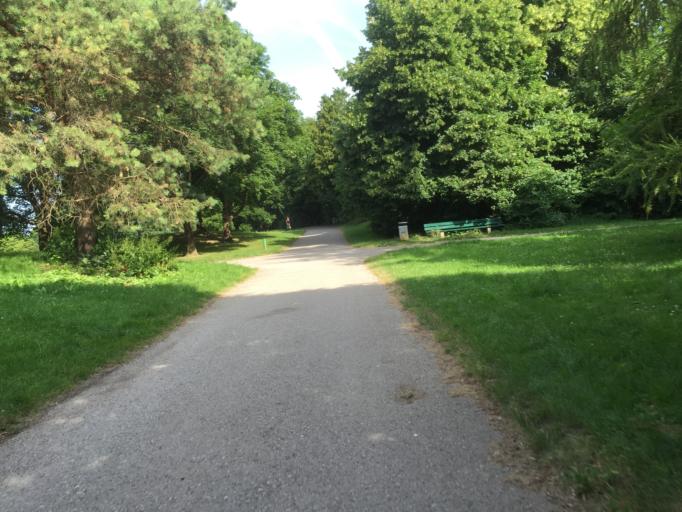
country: DE
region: Bavaria
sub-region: Upper Bavaria
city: Bogenhausen
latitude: 48.1218
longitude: 11.6414
